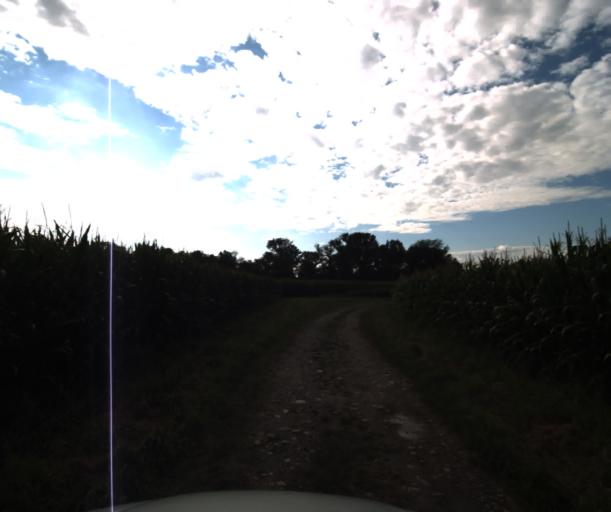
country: FR
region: Midi-Pyrenees
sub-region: Departement de la Haute-Garonne
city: Saubens
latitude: 43.4853
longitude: 1.3454
